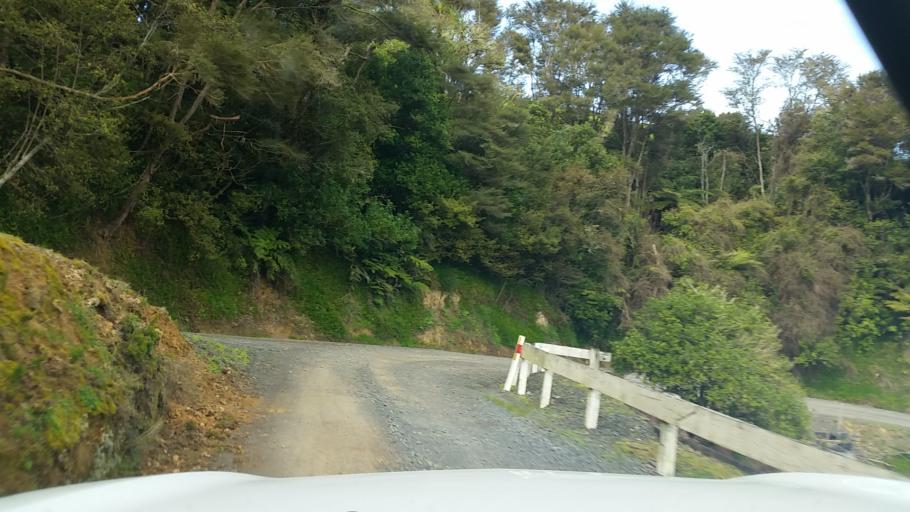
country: NZ
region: Waikato
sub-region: Hauraki District
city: Ngatea
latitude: -37.4805
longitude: 175.4529
